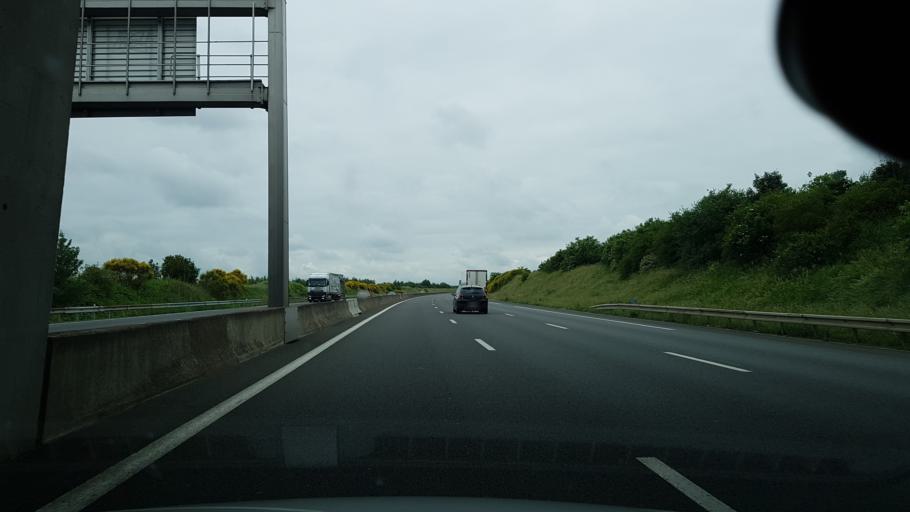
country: FR
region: Centre
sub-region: Departement du Loir-et-Cher
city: Villebarou
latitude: 47.6226
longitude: 1.3424
